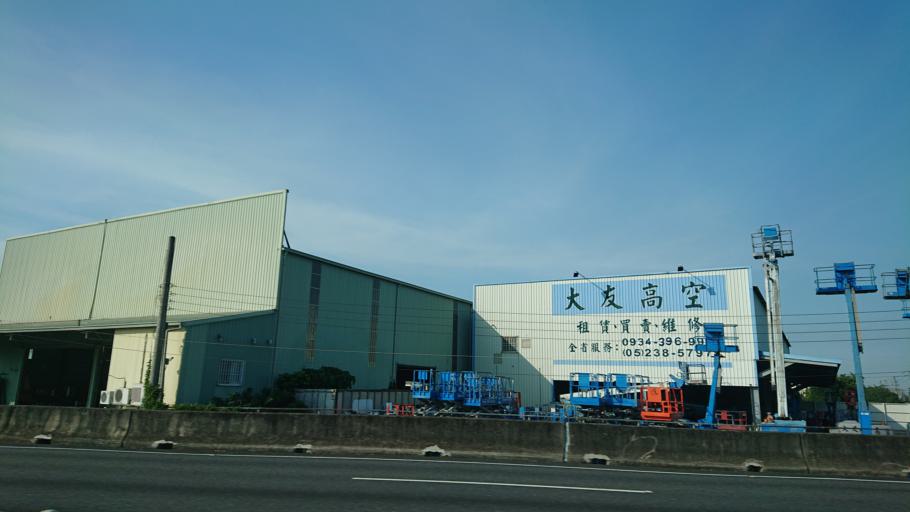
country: TW
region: Taiwan
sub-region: Taichung City
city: Taichung
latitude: 24.2076
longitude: 120.6602
